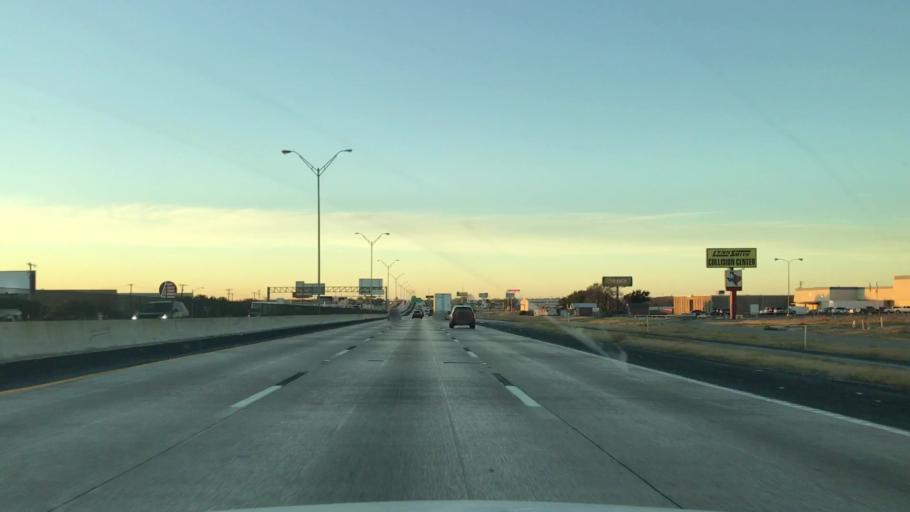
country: US
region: Texas
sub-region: Tarrant County
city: Everman
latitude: 32.6251
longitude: -97.3218
